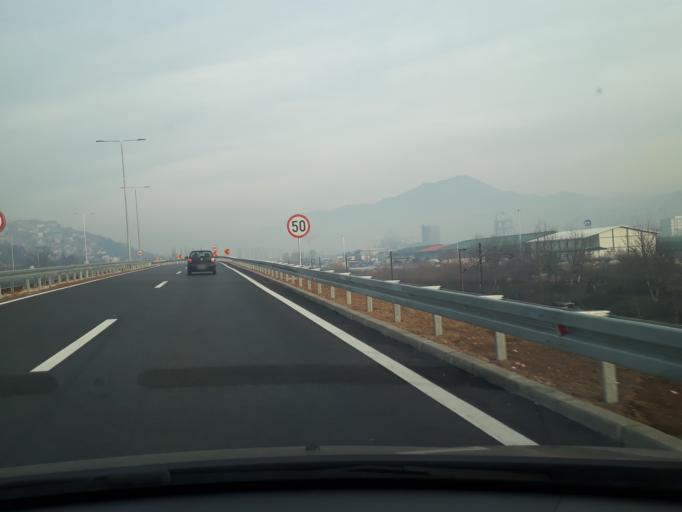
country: BA
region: Federation of Bosnia and Herzegovina
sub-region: Kanton Sarajevo
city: Sarajevo
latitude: 43.8515
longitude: 18.3348
